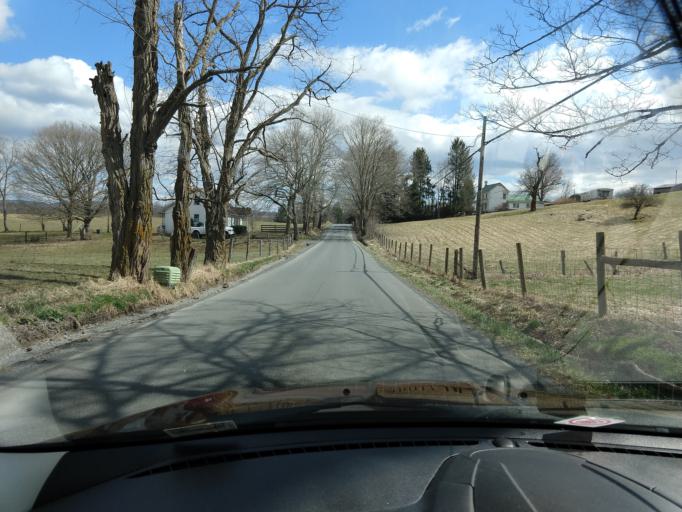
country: US
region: West Virginia
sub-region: Greenbrier County
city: Fairlea
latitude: 37.8113
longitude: -80.5024
